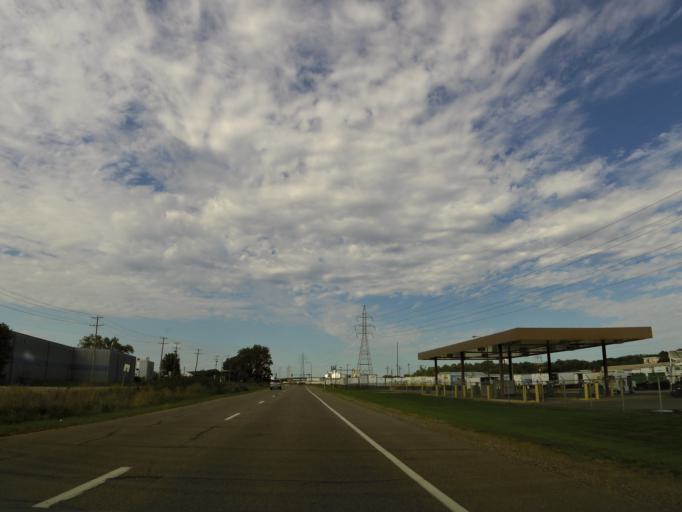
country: US
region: Minnesota
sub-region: Anoka County
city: Columbia Heights
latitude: 45.0332
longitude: -93.2762
